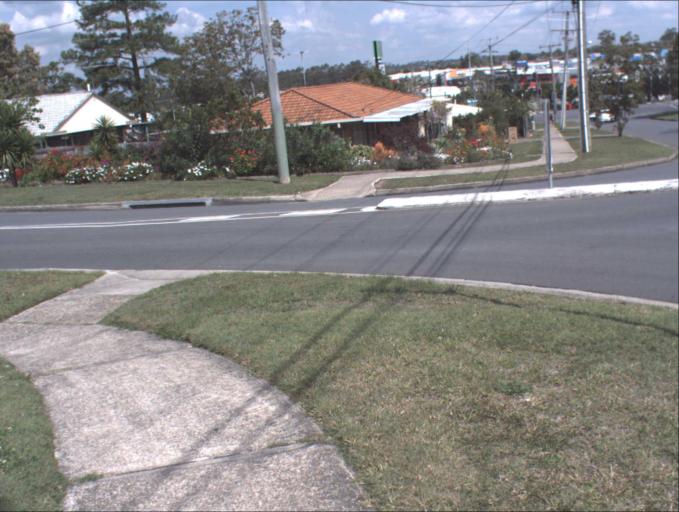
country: AU
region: Queensland
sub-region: Brisbane
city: Sunnybank Hills
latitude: -27.6605
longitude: 153.0461
